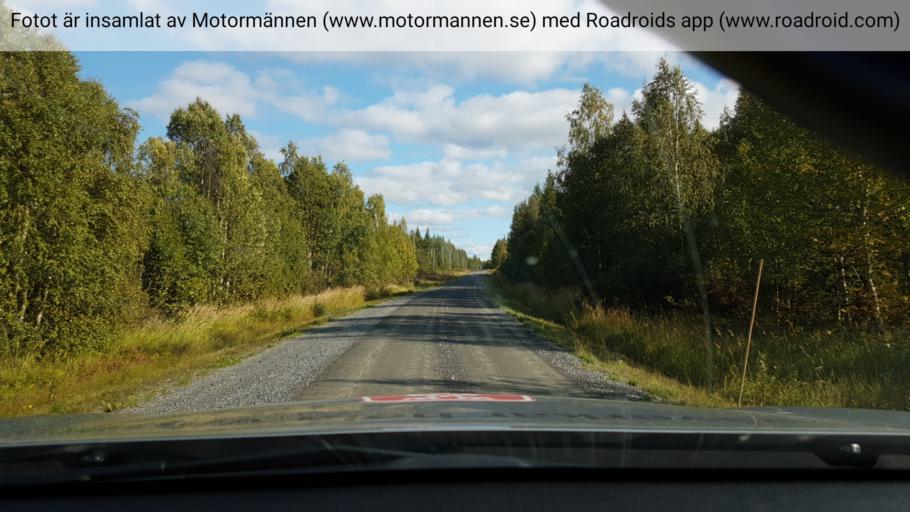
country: SE
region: Vaesterbotten
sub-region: Sorsele Kommun
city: Sorsele
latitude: 65.4746
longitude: 17.6291
